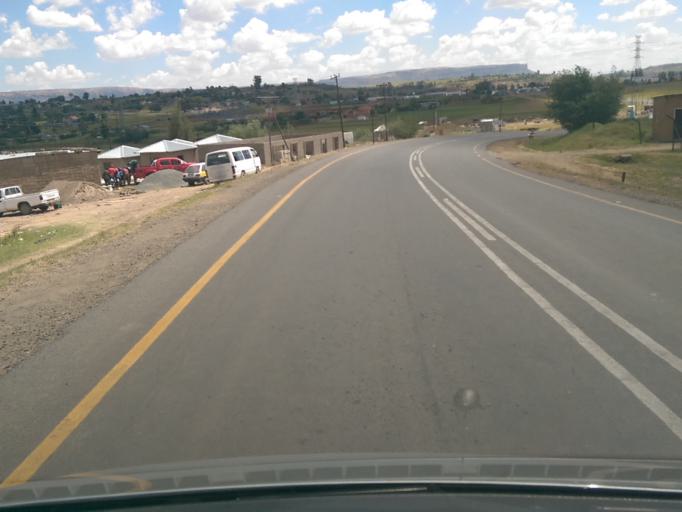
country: LS
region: Maseru
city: Maseru
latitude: -29.4036
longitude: 27.5681
